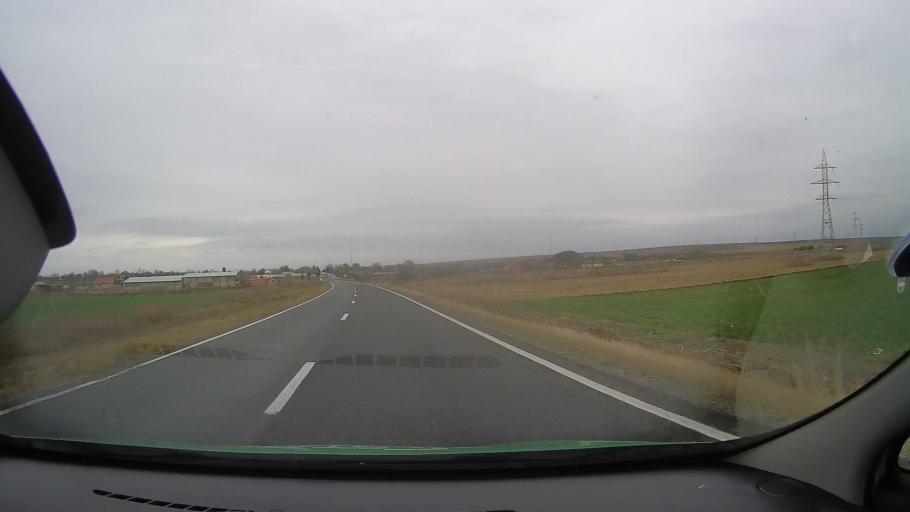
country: RO
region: Constanta
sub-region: Comuna Nicolae Balcescu
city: Dorobantu
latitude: 44.4139
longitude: 28.3182
